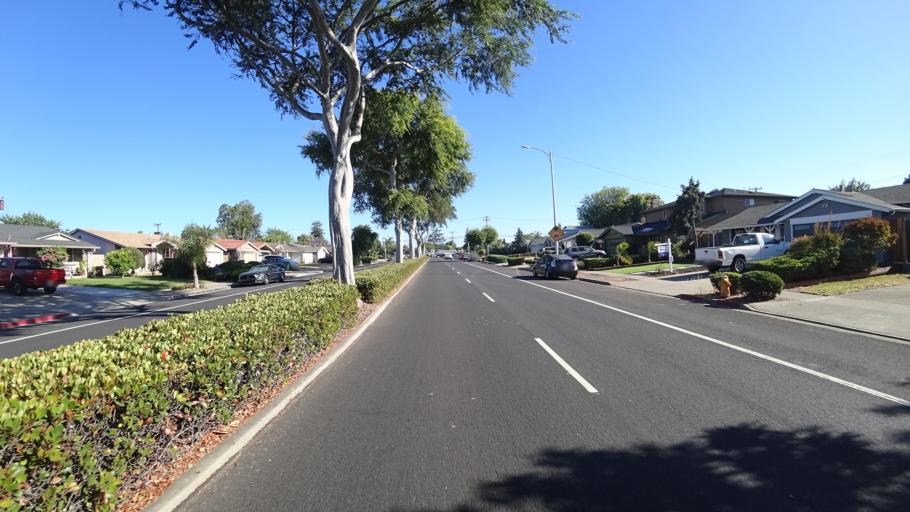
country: US
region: California
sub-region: Alameda County
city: Hayward
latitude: 37.6448
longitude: -122.0991
